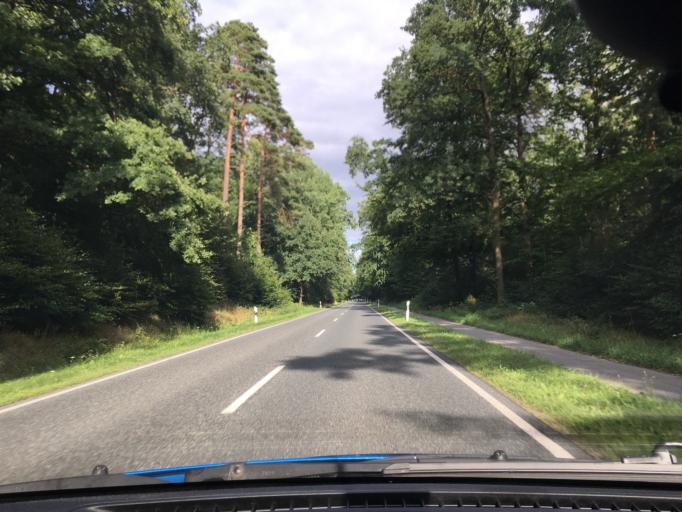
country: DE
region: Lower Saxony
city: Neu Wulmstorf
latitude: 53.4063
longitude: 9.8441
